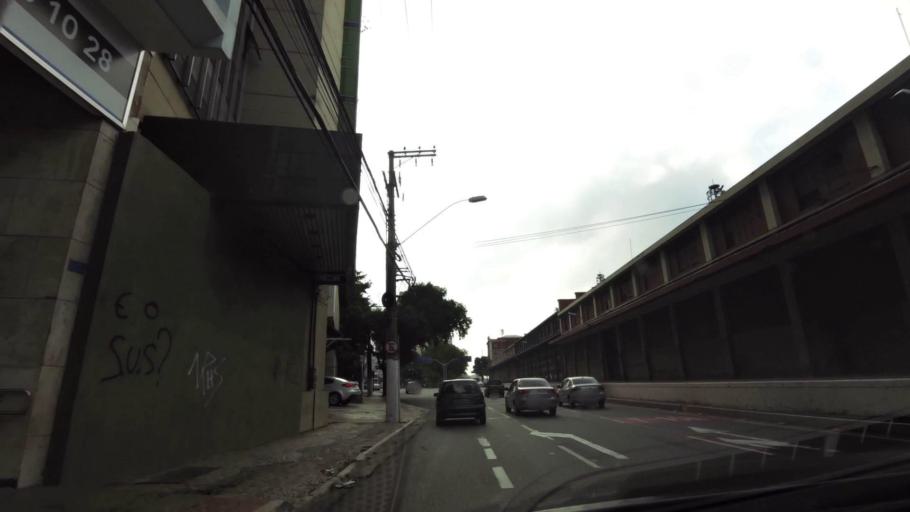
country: BR
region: Espirito Santo
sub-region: Vitoria
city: Vitoria
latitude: -20.3219
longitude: -40.3381
